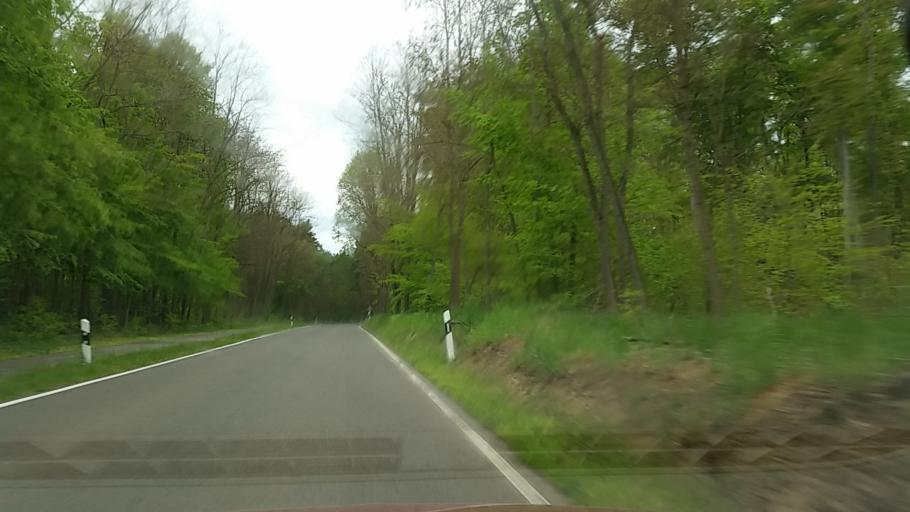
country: DE
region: Brandenburg
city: Reichenwalde
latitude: 52.3086
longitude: 13.9686
